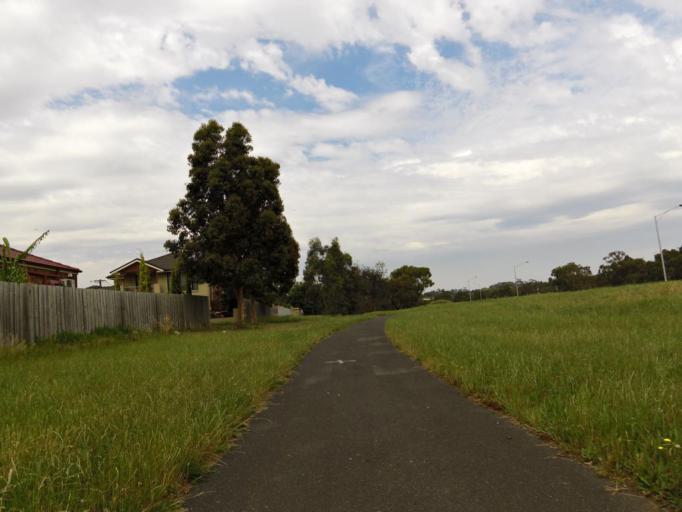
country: AU
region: Victoria
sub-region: Greater Dandenong
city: Springvale South
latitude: -37.9634
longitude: 145.1363
